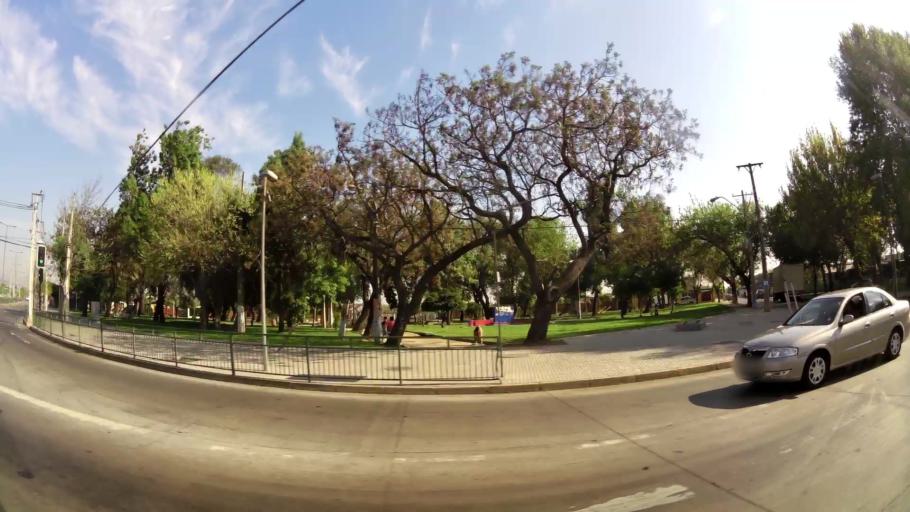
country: CL
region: Santiago Metropolitan
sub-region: Provincia de Santiago
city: Lo Prado
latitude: -33.5118
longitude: -70.7274
